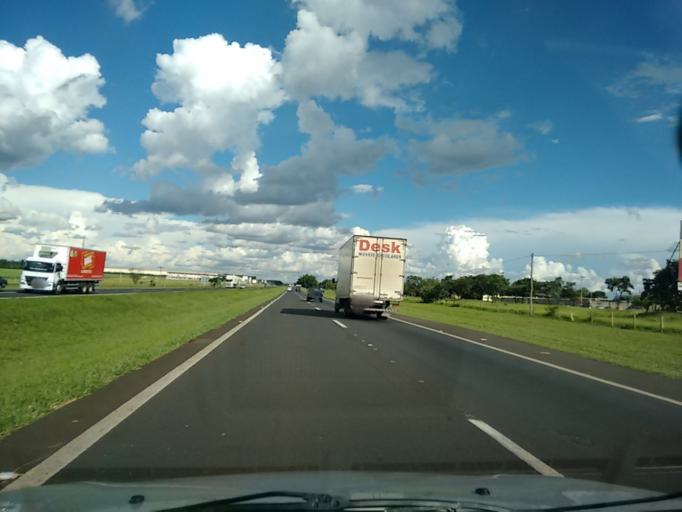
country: BR
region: Sao Paulo
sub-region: Ibate
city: Ibate
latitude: -21.9303
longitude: -48.0211
